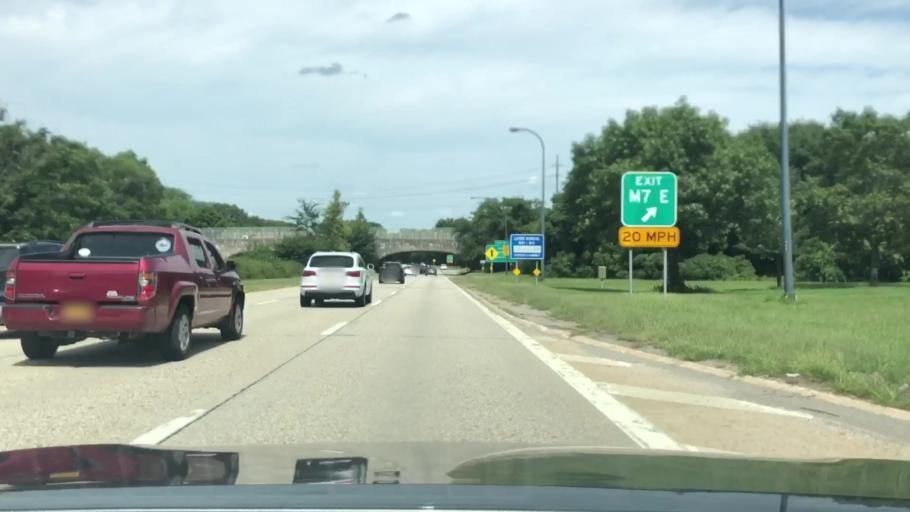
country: US
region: New York
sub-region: Nassau County
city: Freeport
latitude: 40.6637
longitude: -73.5683
